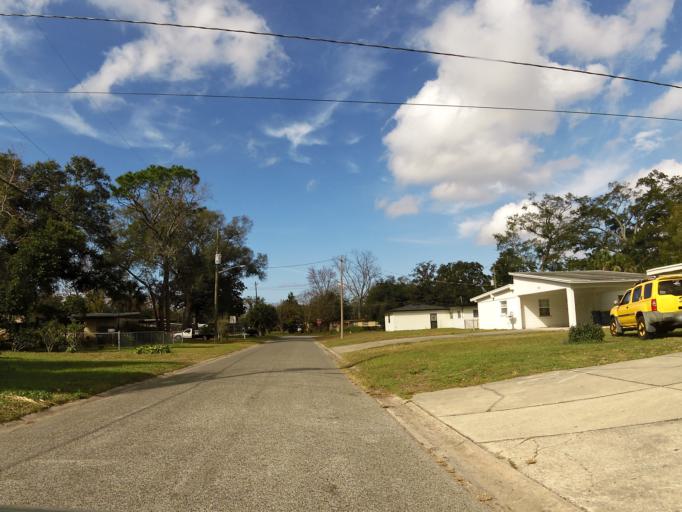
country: US
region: Florida
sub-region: Duval County
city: Jacksonville
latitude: 30.3395
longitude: -81.5838
